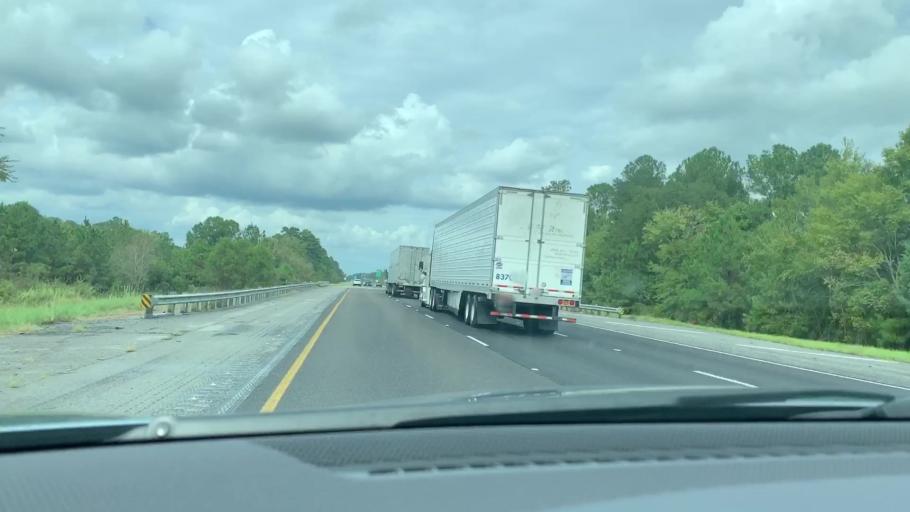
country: US
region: Georgia
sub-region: Liberty County
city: Midway
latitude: 31.7539
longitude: -81.3830
